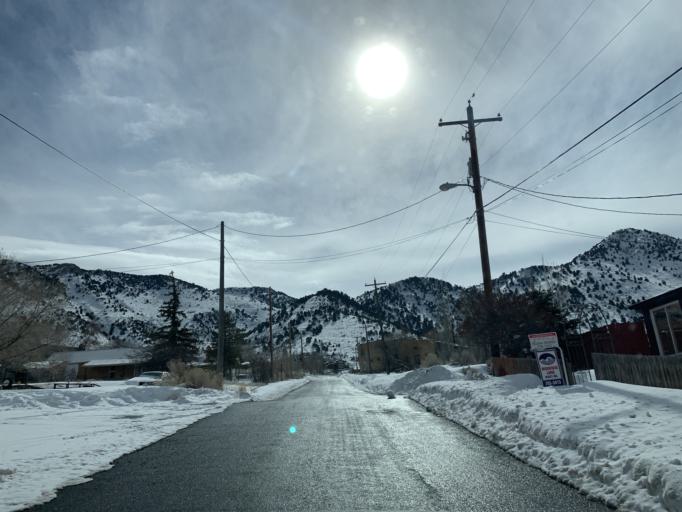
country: US
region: Utah
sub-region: Utah County
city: Genola
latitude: 39.9524
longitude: -112.1171
